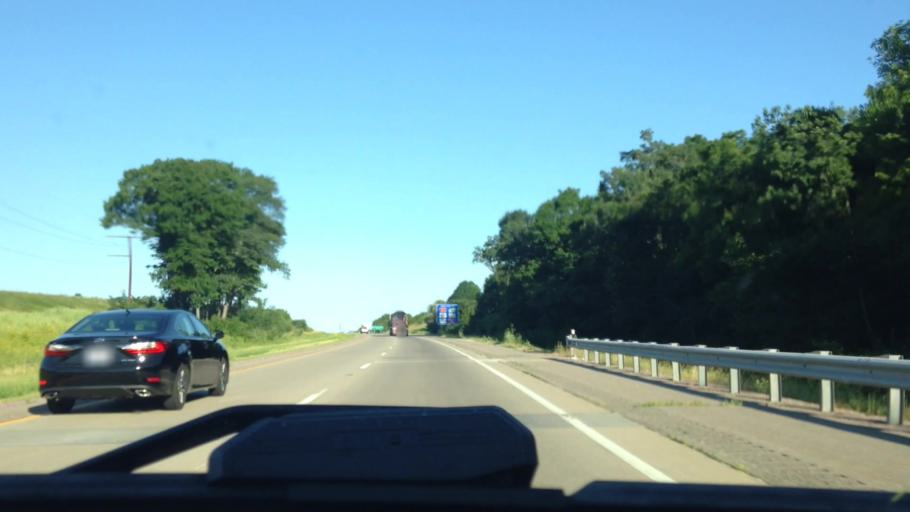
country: US
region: Wisconsin
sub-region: Sauk County
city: Lake Delton
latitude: 43.5672
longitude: -89.7510
